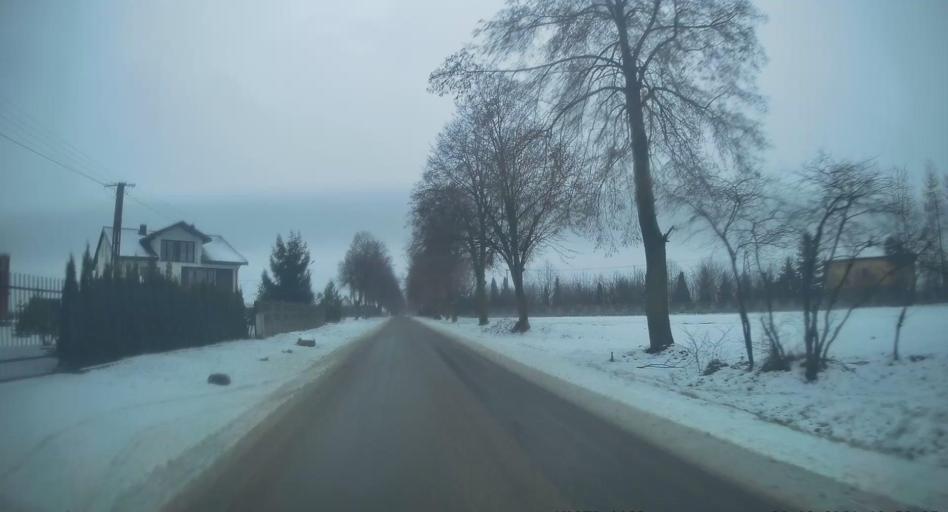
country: PL
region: Lodz Voivodeship
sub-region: Powiat tomaszowski
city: Czerniewice
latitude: 51.6902
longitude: 20.2169
